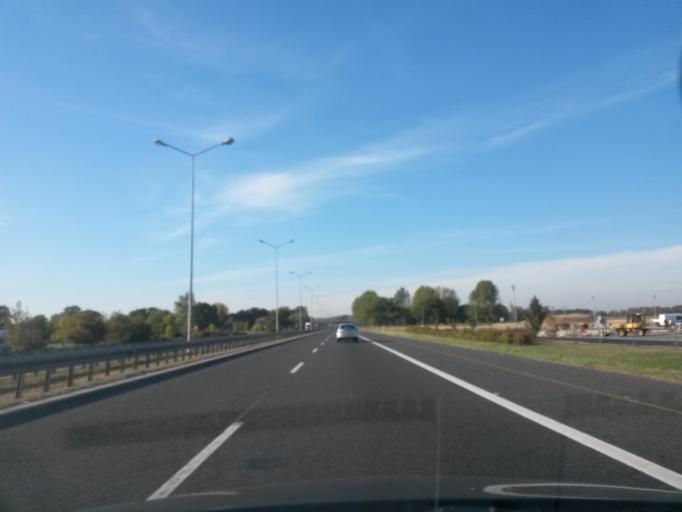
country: PL
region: Lower Silesian Voivodeship
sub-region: Powiat wroclawski
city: Zorawina
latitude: 50.9559
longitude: 17.0780
